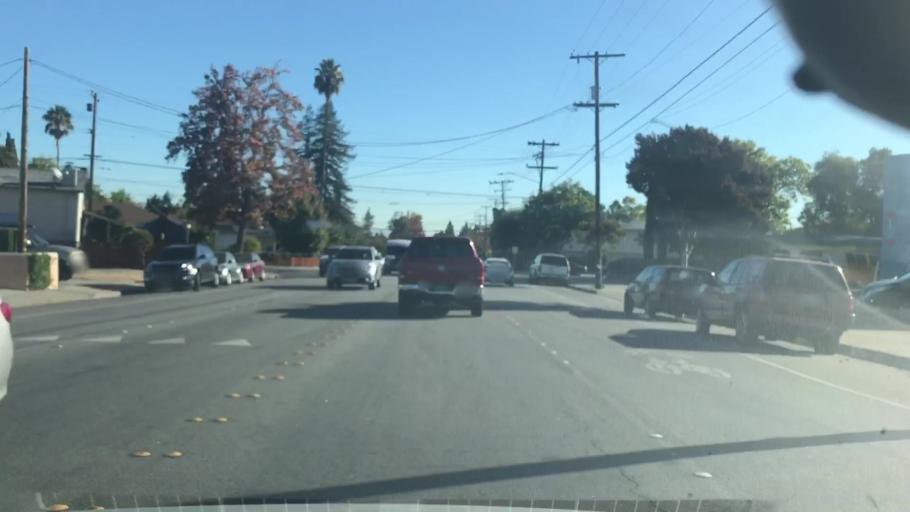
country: US
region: California
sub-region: San Mateo County
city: Redwood City
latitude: 37.4702
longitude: -122.2460
